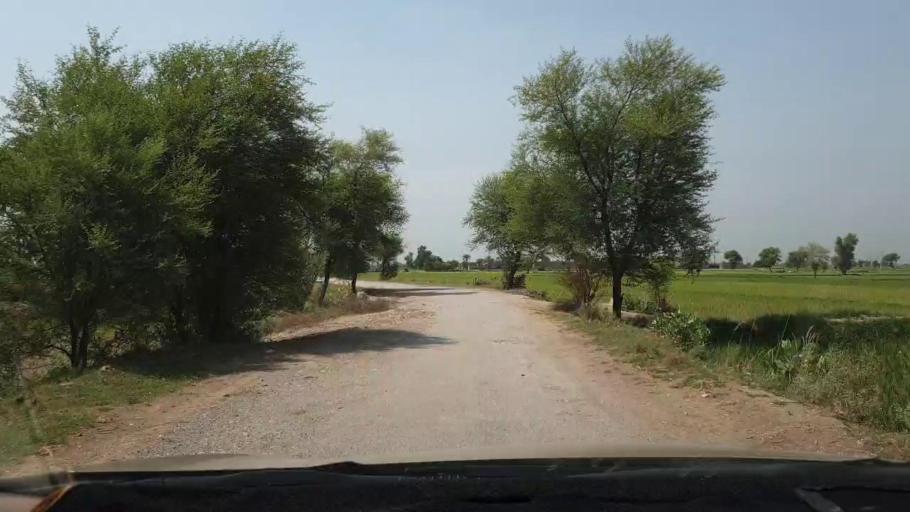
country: PK
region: Sindh
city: Naudero
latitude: 27.6415
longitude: 68.2740
